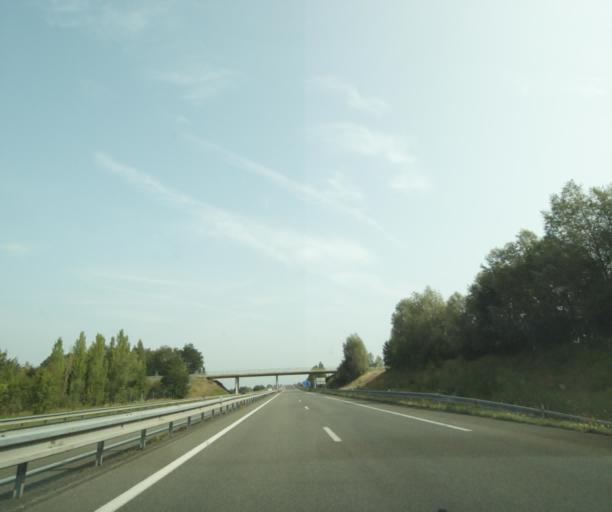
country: FR
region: Pays de la Loire
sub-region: Departement de la Sarthe
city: Montbizot
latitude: 48.1982
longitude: 0.1734
